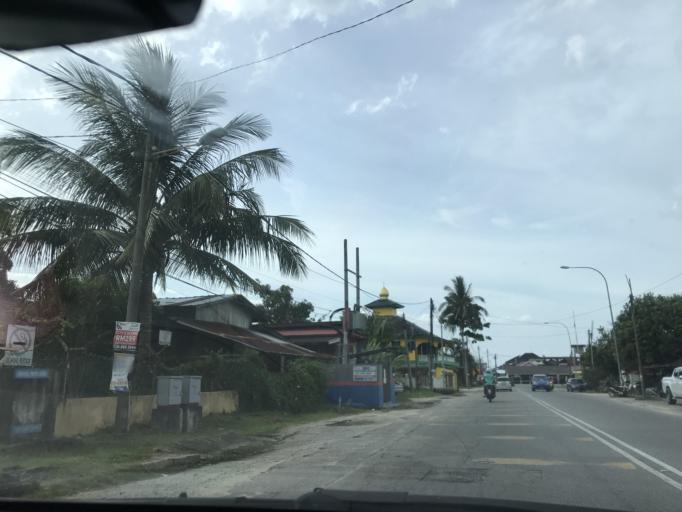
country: MY
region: Kelantan
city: Kota Bharu
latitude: 6.1015
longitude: 102.2307
